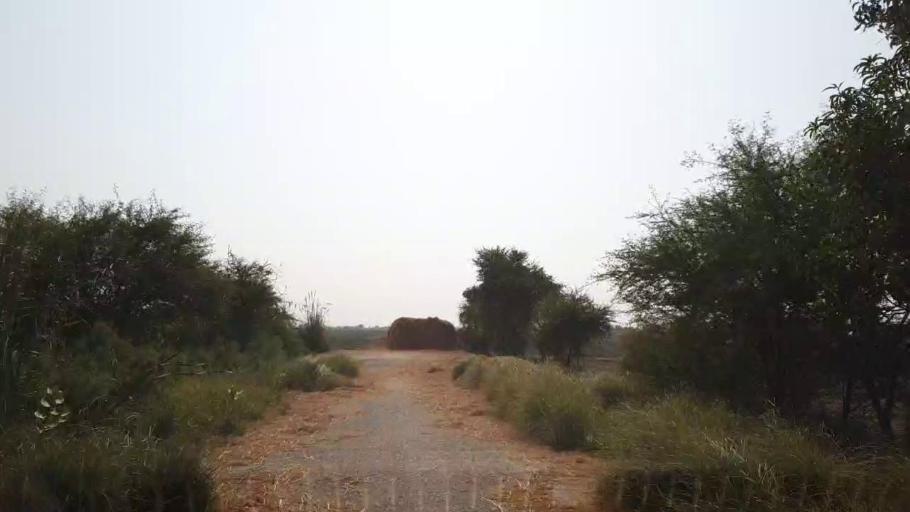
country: PK
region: Sindh
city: Bulri
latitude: 24.9541
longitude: 68.3279
